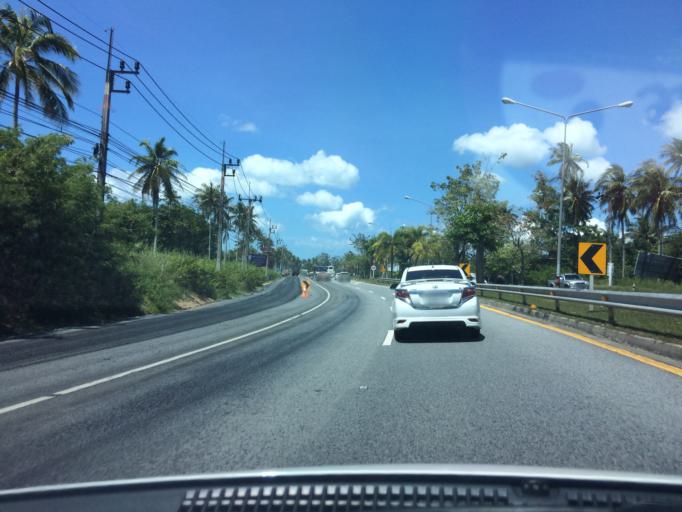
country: TH
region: Phuket
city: Thalang
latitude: 8.1649
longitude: 98.3036
